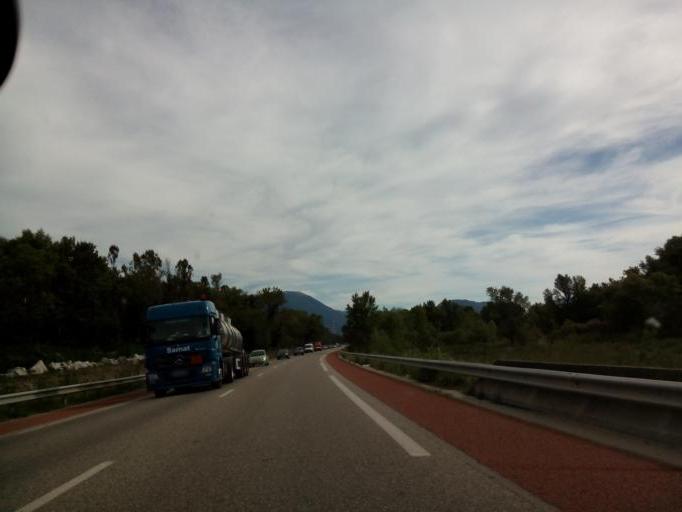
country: FR
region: Rhone-Alpes
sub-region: Departement de l'Isere
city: Le Pont-de-Claix
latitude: 45.1156
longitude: 5.6989
